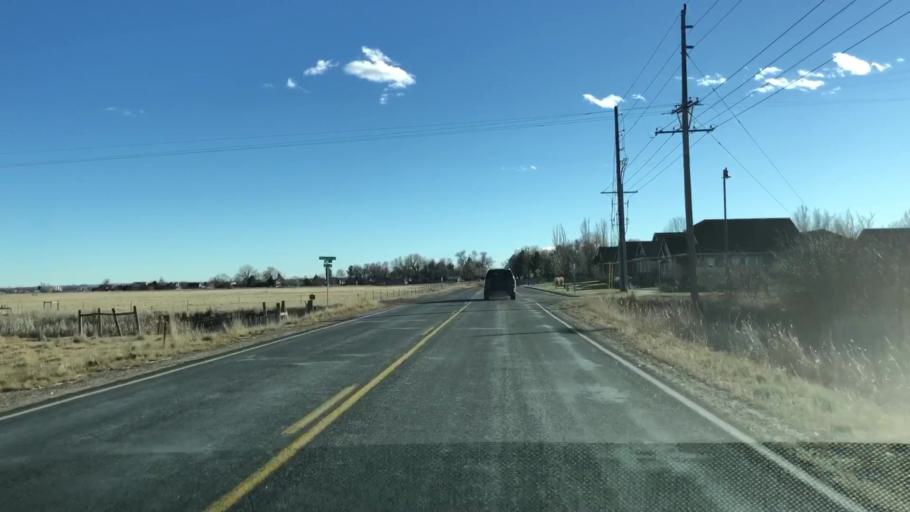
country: US
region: Colorado
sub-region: Weld County
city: Windsor
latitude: 40.5379
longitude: -104.9824
